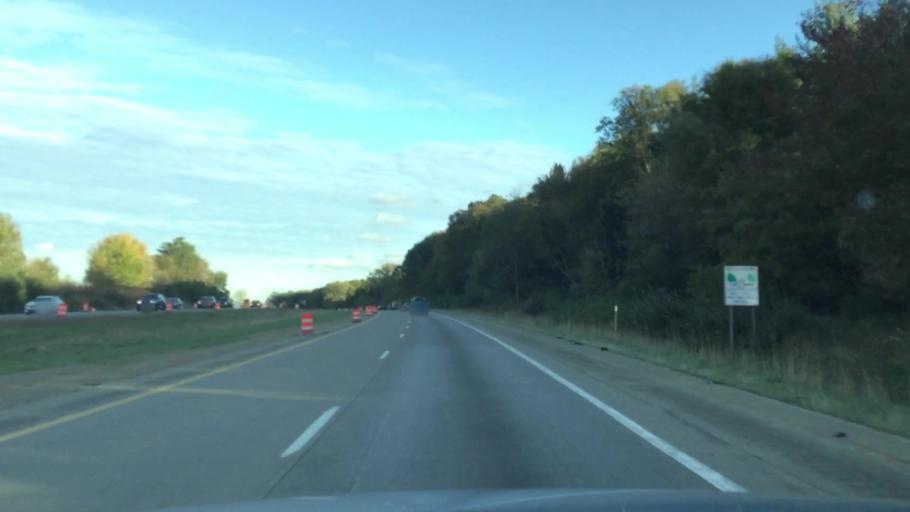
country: US
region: Michigan
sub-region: Calhoun County
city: Marshall
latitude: 42.2844
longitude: -84.9481
